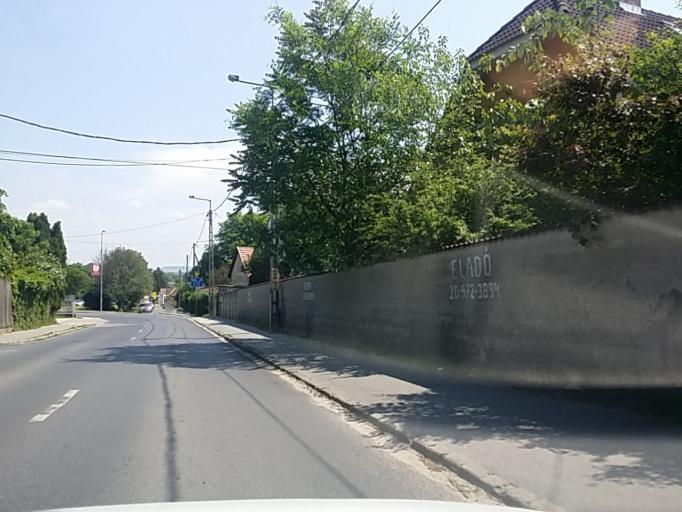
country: HU
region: Pest
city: Szentendre
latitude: 47.6647
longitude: 19.0701
